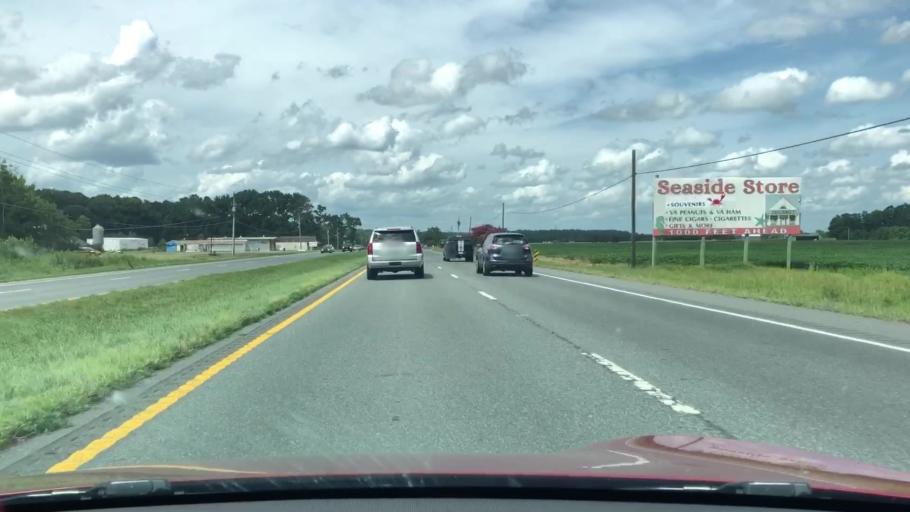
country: US
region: Virginia
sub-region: Accomack County
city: Wattsville
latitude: 37.9062
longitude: -75.5483
